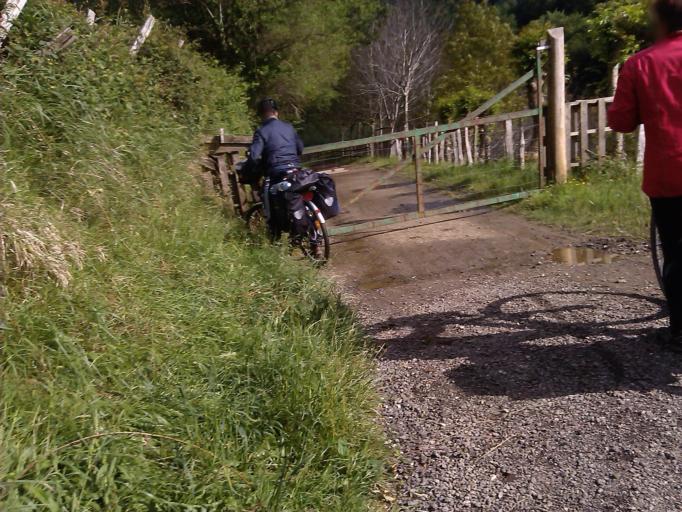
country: ES
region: Navarre
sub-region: Provincia de Navarra
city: Leitza
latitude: 43.0575
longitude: -1.9013
